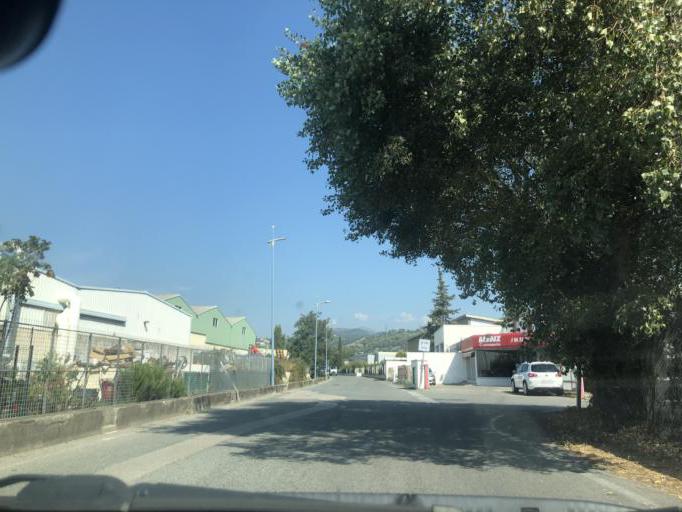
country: FR
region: Provence-Alpes-Cote d'Azur
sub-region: Departement des Alpes-Maritimes
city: Castagniers
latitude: 43.7801
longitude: 7.2119
